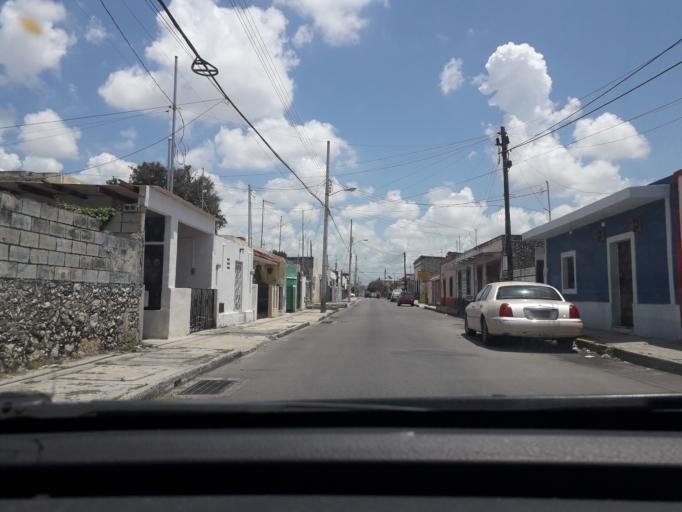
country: MX
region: Yucatan
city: Merida
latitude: 20.9536
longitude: -89.6208
